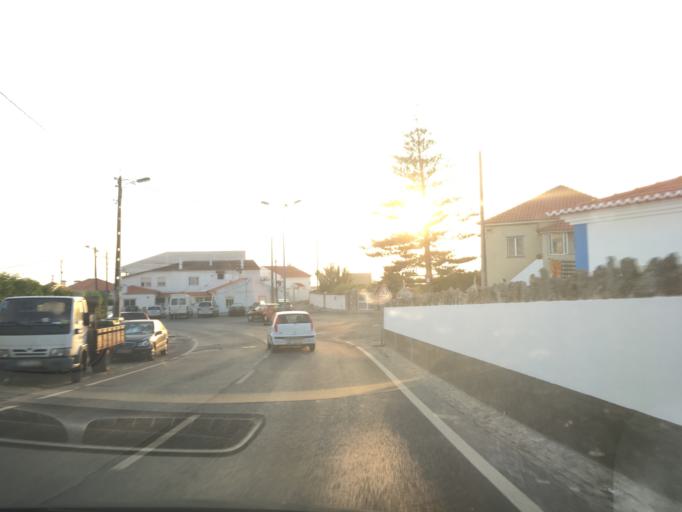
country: PT
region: Lisbon
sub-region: Sintra
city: Colares
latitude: 38.8384
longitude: -9.4613
